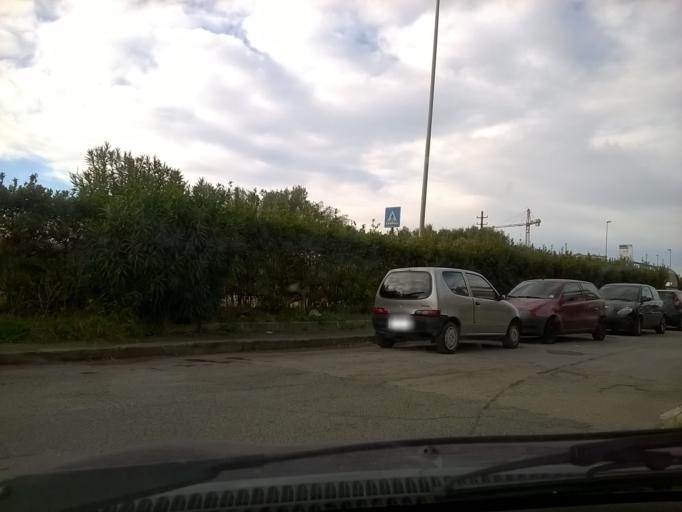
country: IT
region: Apulia
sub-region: Provincia di Taranto
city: Taranto
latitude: 40.4328
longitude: 17.2653
